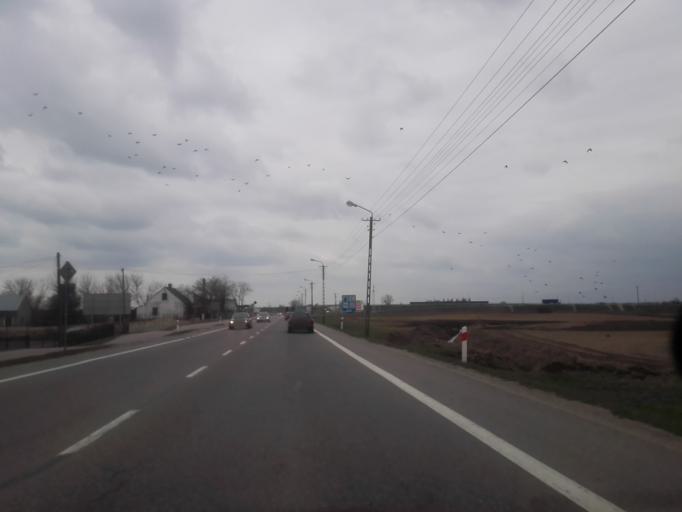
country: PL
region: Podlasie
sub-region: Powiat augustowski
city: Augustow
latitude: 53.8347
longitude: 22.9674
